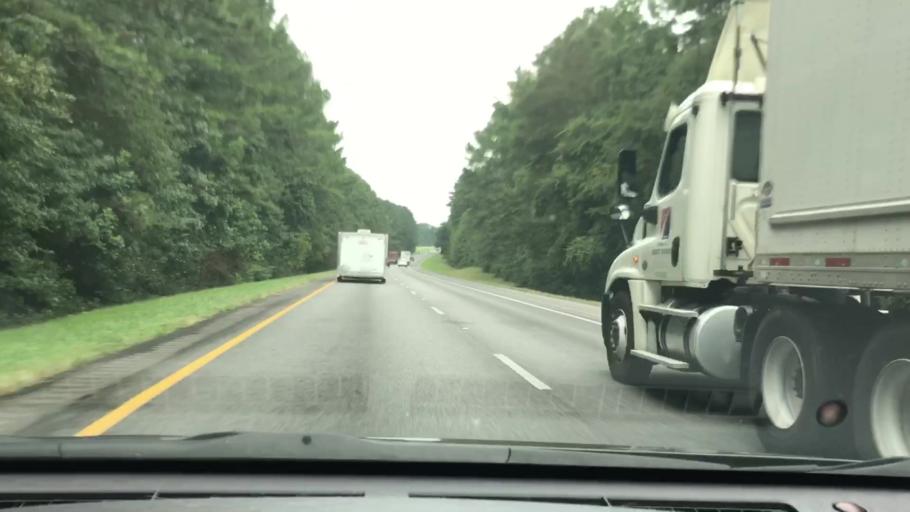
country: US
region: Georgia
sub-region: Morgan County
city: Madison
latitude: 33.5765
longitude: -83.5638
